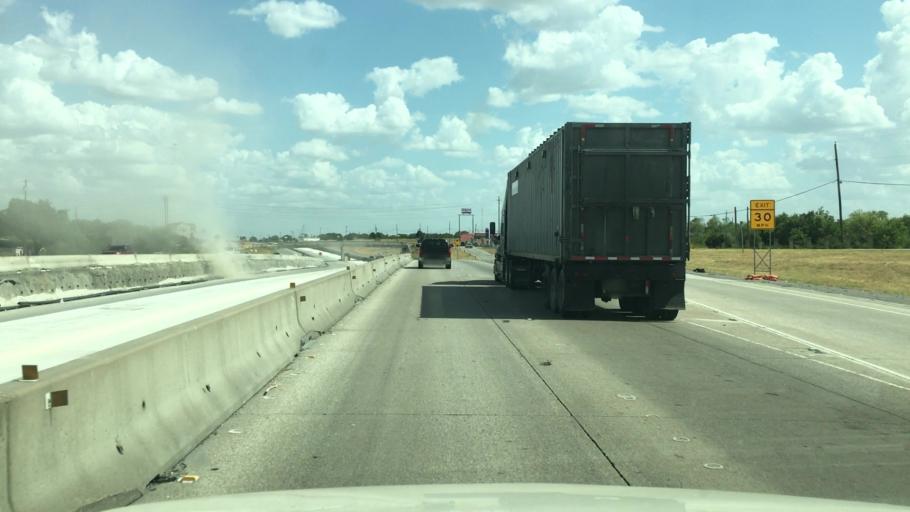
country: US
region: Texas
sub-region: Ellis County
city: Waxahachie
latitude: 32.3775
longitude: -96.8651
